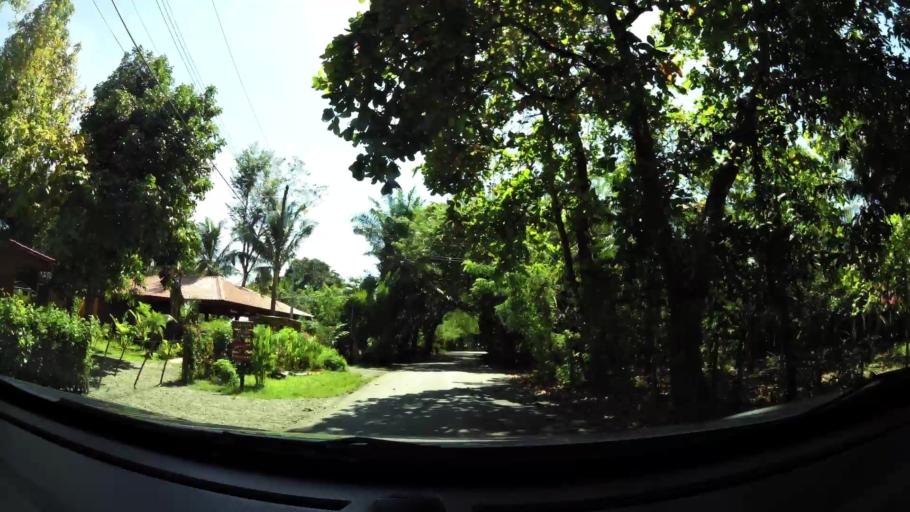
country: CR
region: Puntarenas
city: Quepos
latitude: 9.3204
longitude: -83.9584
